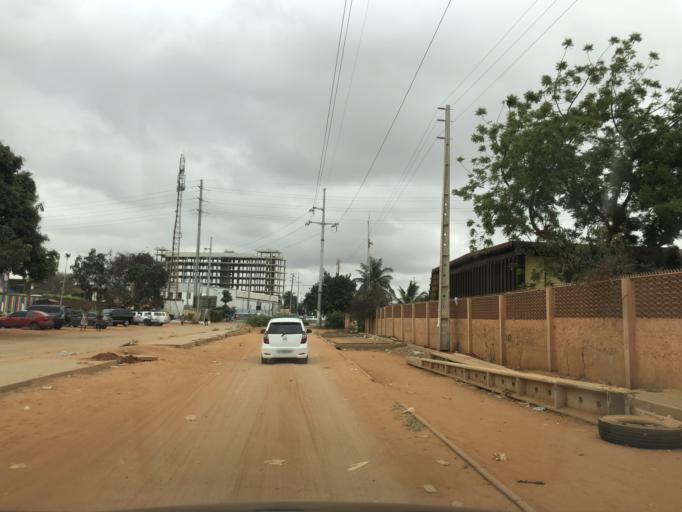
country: AO
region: Luanda
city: Luanda
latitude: -8.9013
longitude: 13.1981
